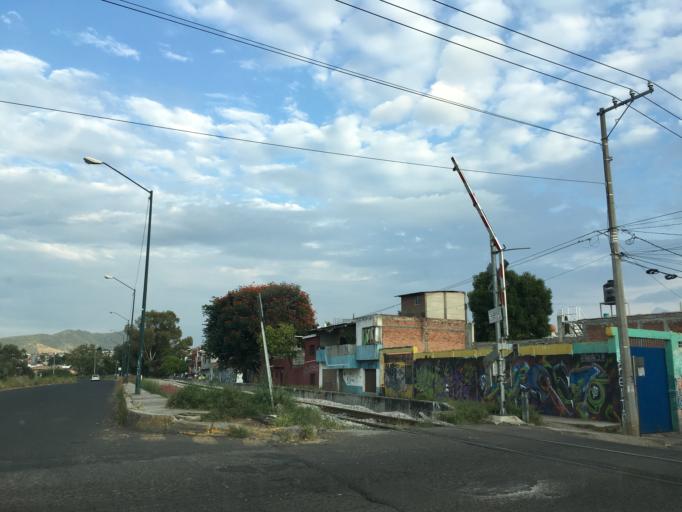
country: MX
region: Michoacan
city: Morelia
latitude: 19.7123
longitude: -101.1940
